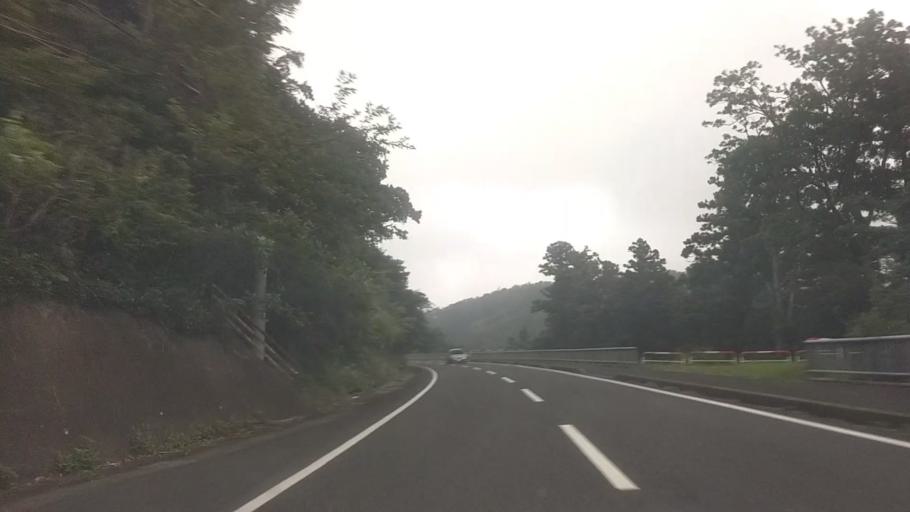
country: JP
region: Chiba
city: Kawaguchi
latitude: 35.1441
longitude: 140.1508
